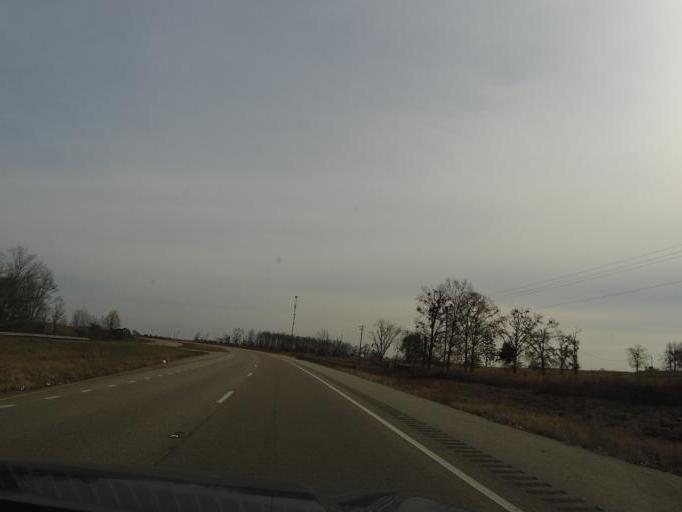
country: US
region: Alabama
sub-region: Houston County
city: Ashford
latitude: 31.1353
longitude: -85.1403
